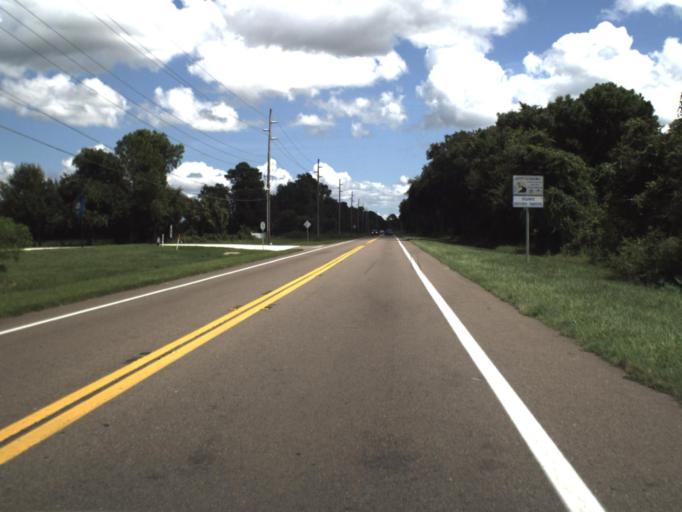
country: US
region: Florida
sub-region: Polk County
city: Lake Alfred
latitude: 28.0697
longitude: -81.6982
